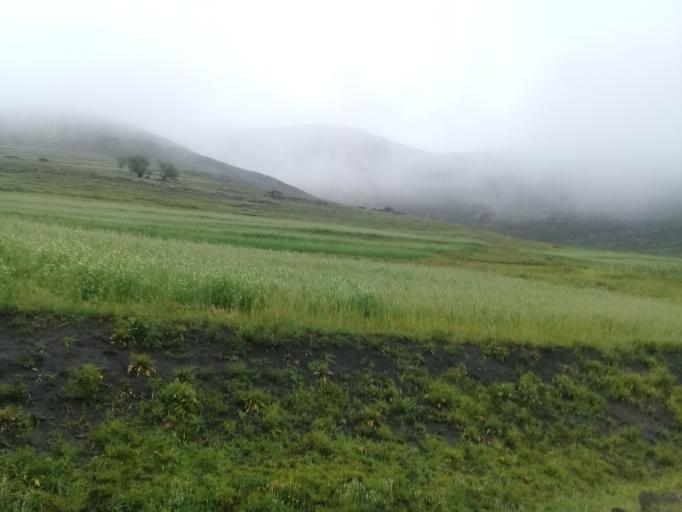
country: LS
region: Mokhotlong
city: Mokhotlong
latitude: -29.3907
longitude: 28.9666
